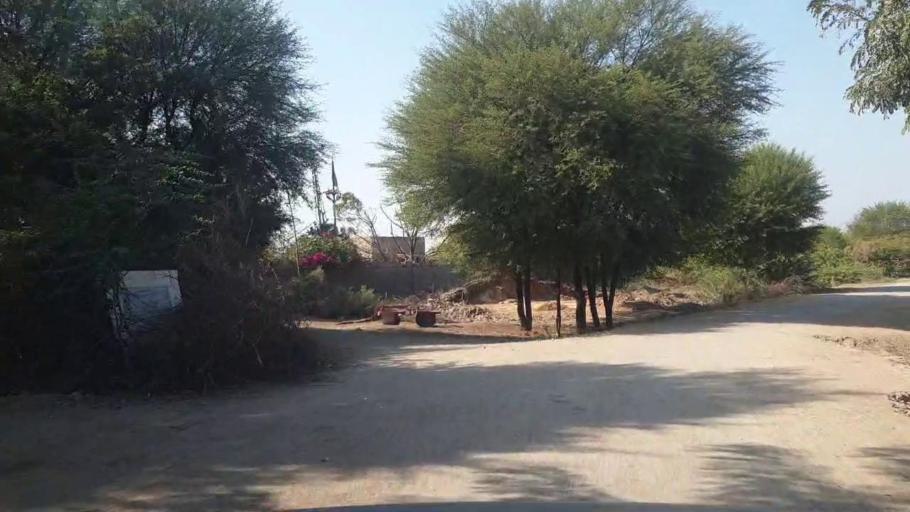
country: PK
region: Sindh
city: Chambar
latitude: 25.3136
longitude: 68.8423
